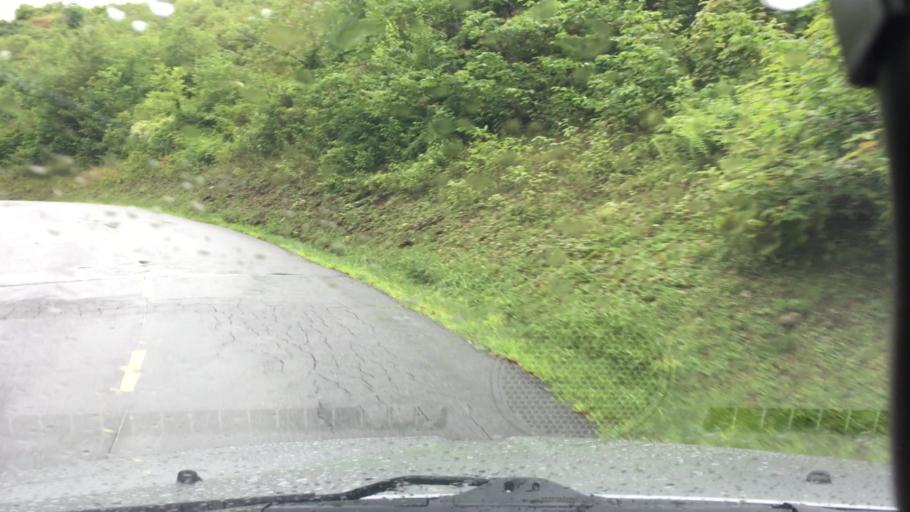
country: US
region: North Carolina
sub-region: Madison County
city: Mars Hill
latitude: 35.9459
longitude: -82.5116
